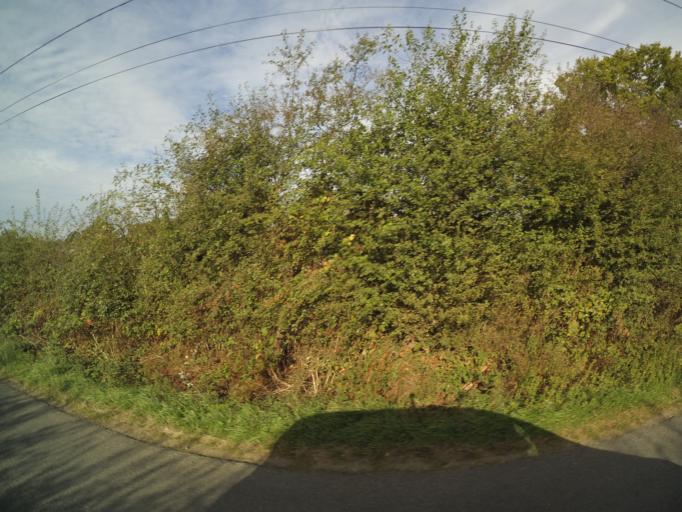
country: FR
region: Pays de la Loire
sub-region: Departement de Maine-et-Loire
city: Geste
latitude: 47.1744
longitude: -1.1219
